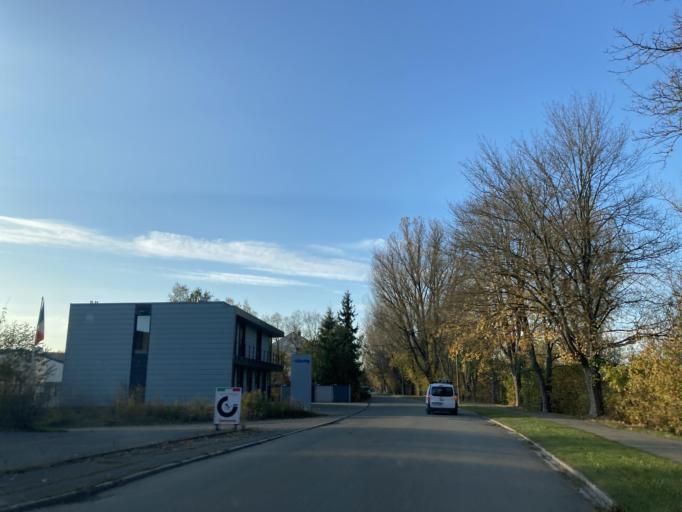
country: DE
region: Baden-Wuerttemberg
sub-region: Freiburg Region
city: Villingen-Schwenningen
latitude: 48.0464
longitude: 8.4675
